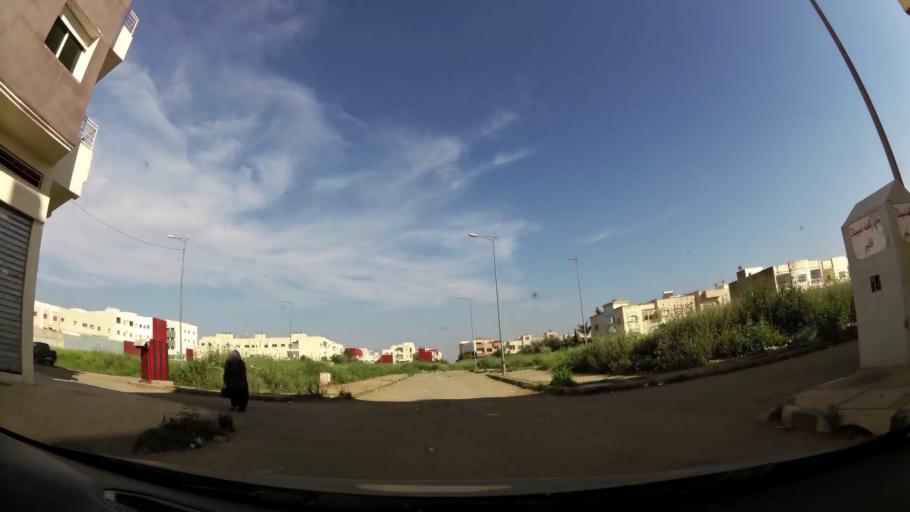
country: MA
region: Fes-Boulemane
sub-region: Fes
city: Fes
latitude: 34.0226
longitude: -5.0289
